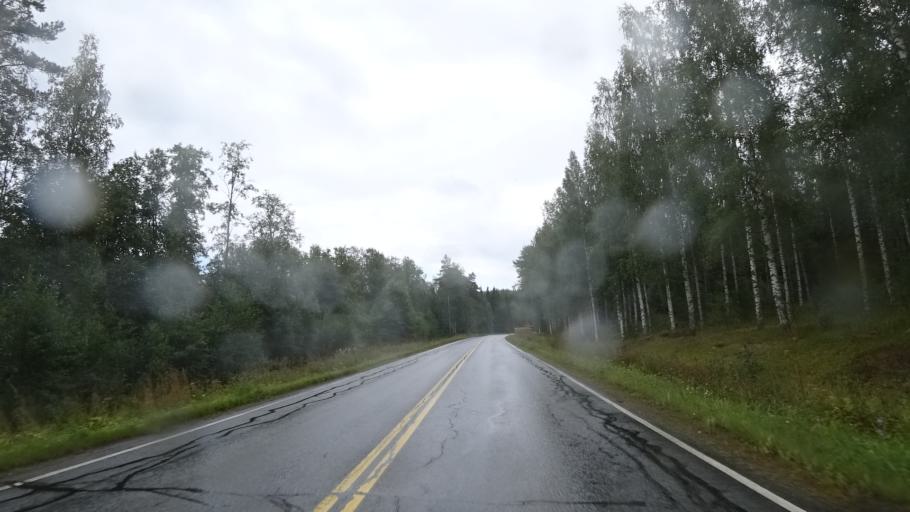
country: FI
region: North Karelia
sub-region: Keski-Karjala
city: Raeaekkylae
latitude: 62.0489
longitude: 29.5768
